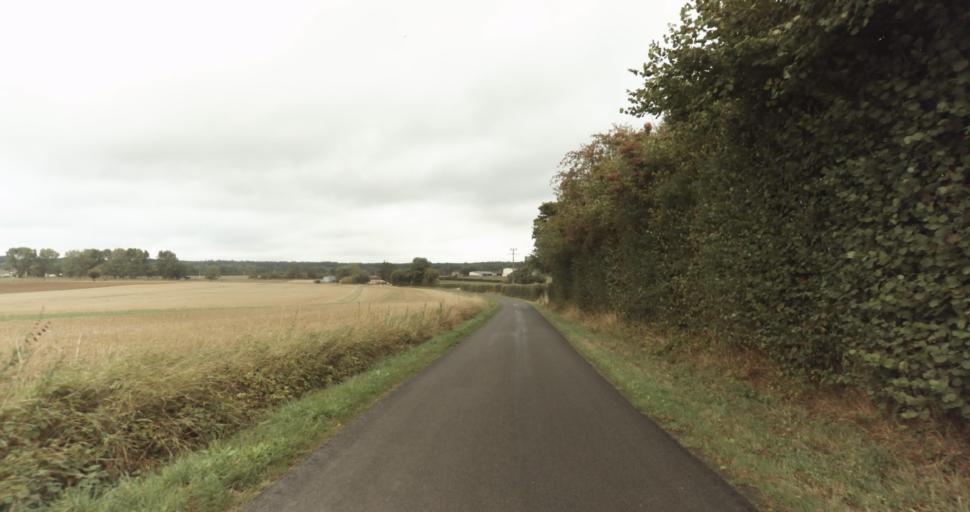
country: FR
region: Lower Normandy
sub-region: Departement de l'Orne
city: Sainte-Gauburge-Sainte-Colombe
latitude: 48.7376
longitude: 0.4700
